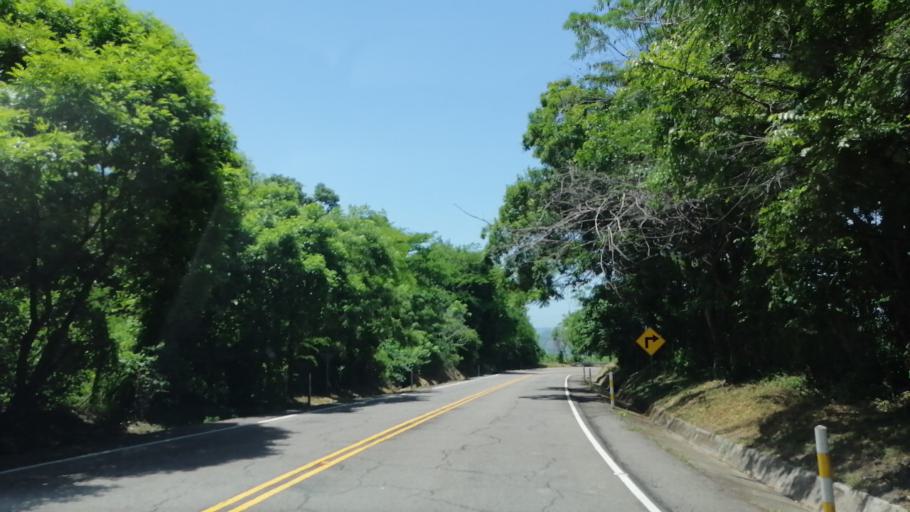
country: SV
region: Chalatenango
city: Nueva Concepcion
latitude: 14.1751
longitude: -89.3111
